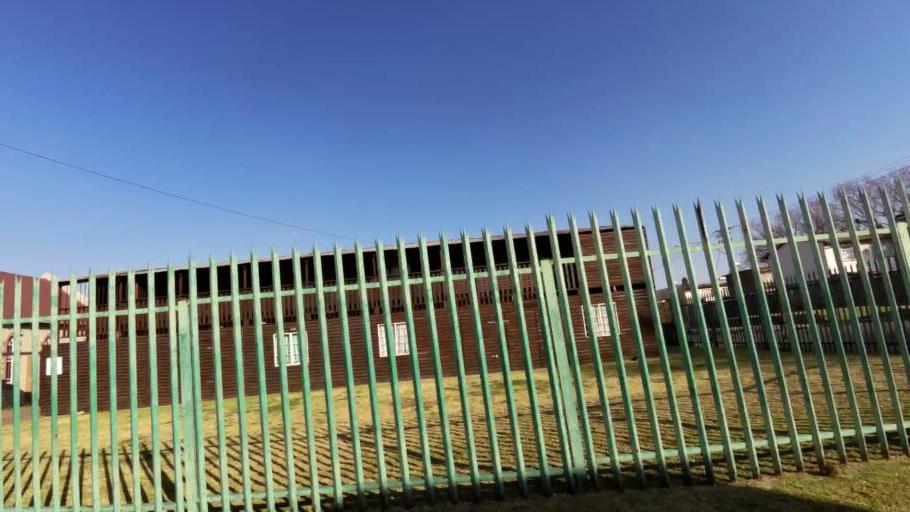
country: ZA
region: Gauteng
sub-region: City of Johannesburg Metropolitan Municipality
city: Johannesburg
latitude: -26.1933
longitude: 28.0150
